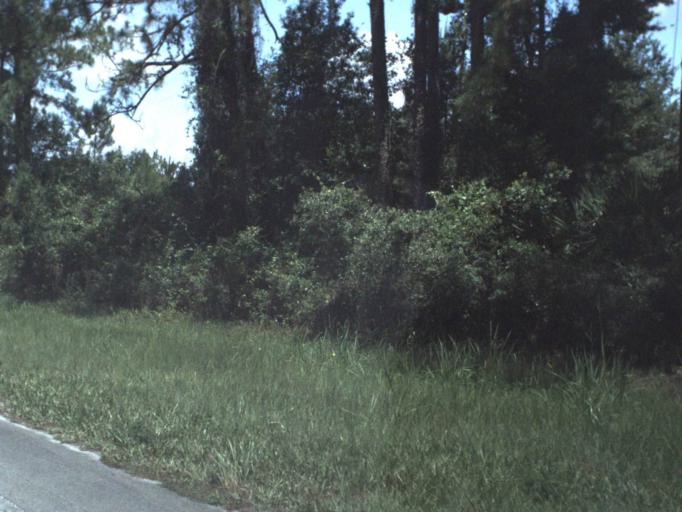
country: US
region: Florida
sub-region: Bradford County
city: Starke
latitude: 29.9385
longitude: -82.0323
